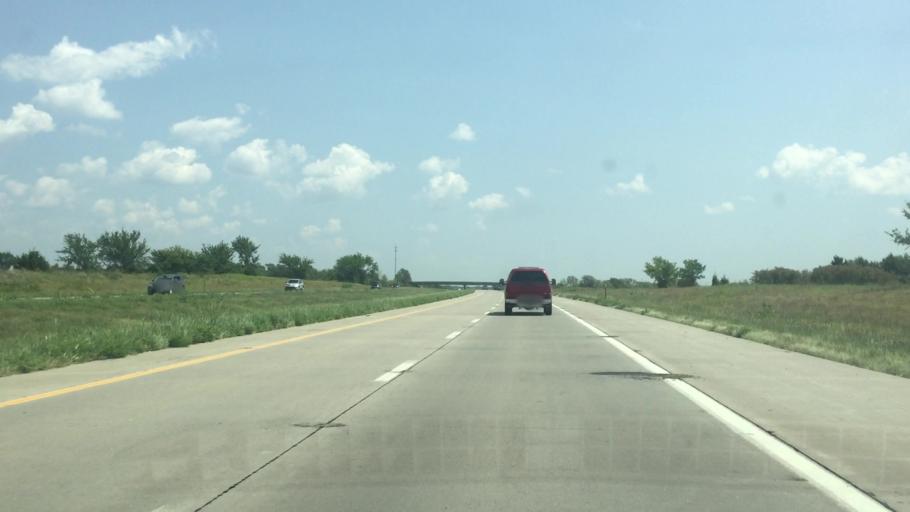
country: US
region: Kansas
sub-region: Franklin County
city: Wellsville
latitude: 38.6813
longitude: -95.1271
